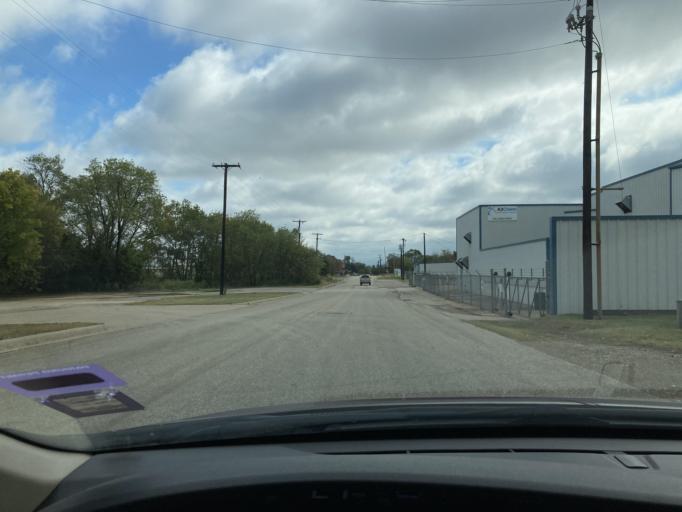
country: US
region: Texas
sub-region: Navarro County
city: Corsicana
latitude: 32.0906
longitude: -96.4632
